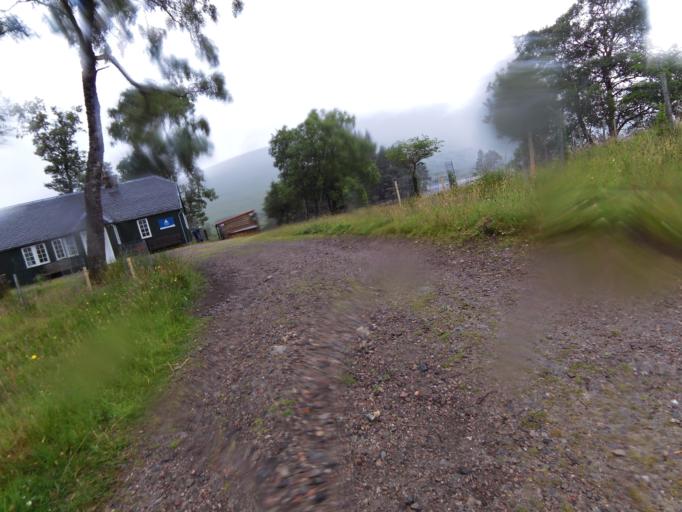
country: GB
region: Scotland
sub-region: Highland
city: Spean Bridge
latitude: 56.7666
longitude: -4.6659
